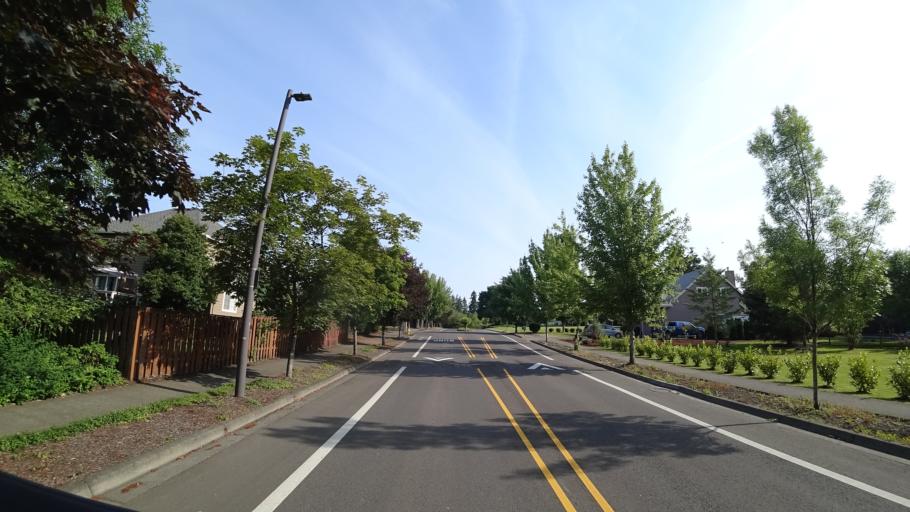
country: US
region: Oregon
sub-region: Clackamas County
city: Happy Valley
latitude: 45.4455
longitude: -122.5248
